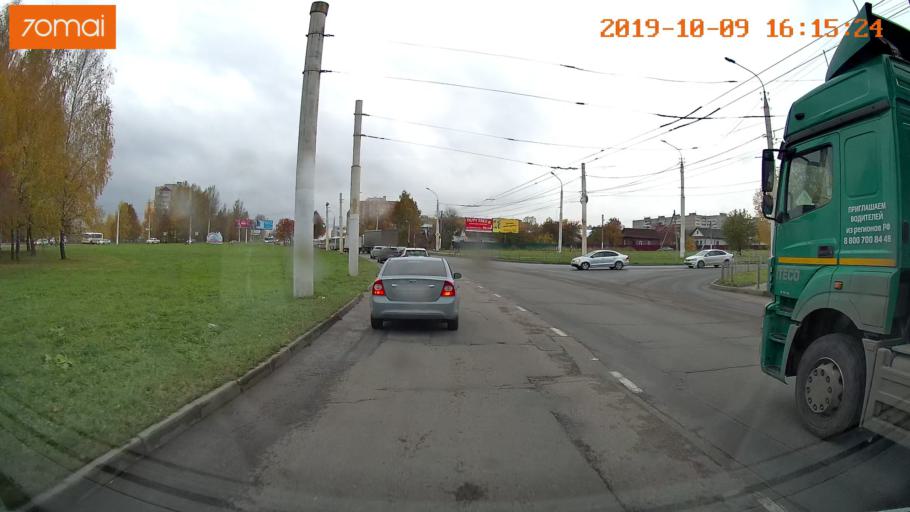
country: RU
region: Kostroma
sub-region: Kostromskoy Rayon
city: Kostroma
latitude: 57.7402
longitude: 40.9164
